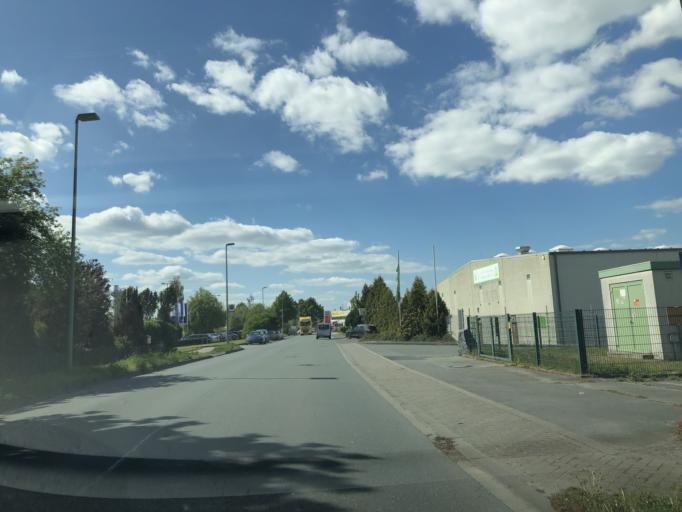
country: DE
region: North Rhine-Westphalia
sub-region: Regierungsbezirk Arnsberg
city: Bad Sassendorf
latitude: 51.5560
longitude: 8.1462
